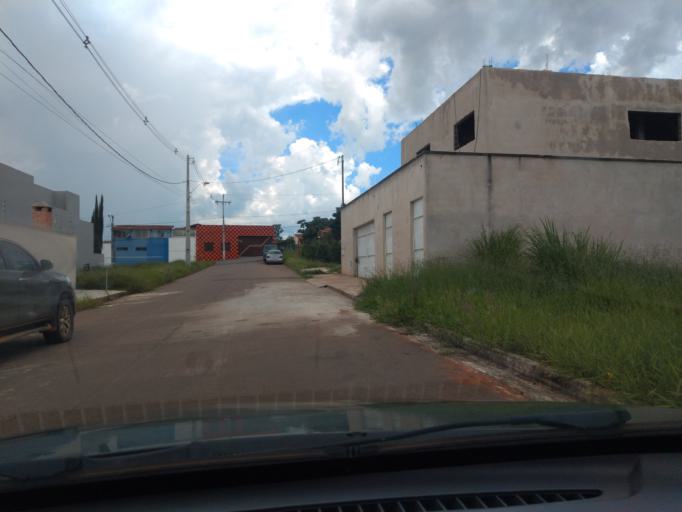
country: BR
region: Minas Gerais
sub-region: Tres Coracoes
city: Tres Coracoes
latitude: -21.6841
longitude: -45.2622
